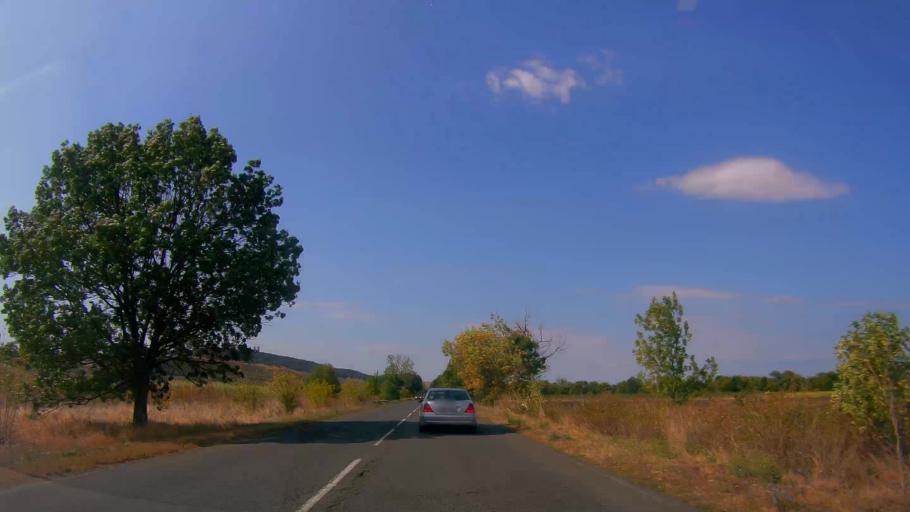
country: BG
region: Burgas
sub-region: Obshtina Karnobat
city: Karnobat
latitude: 42.6595
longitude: 27.0212
